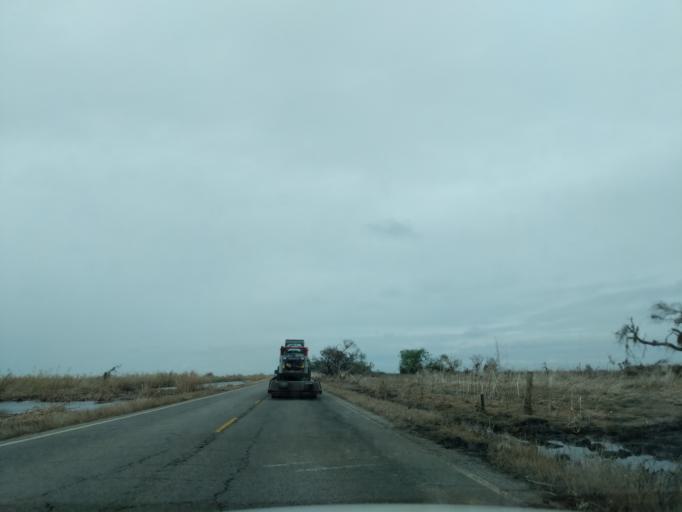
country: US
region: Louisiana
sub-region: Cameron Parish
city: Cameron
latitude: 29.7822
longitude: -93.0751
